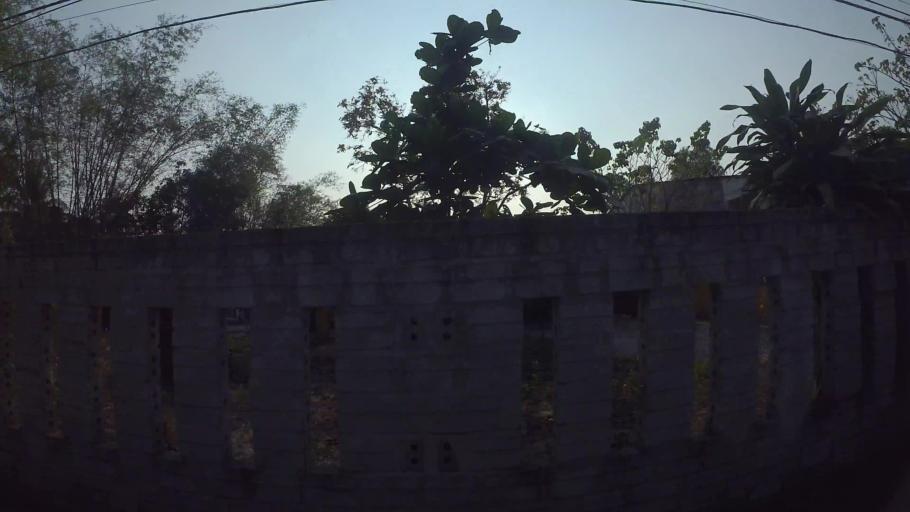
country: VN
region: Da Nang
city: Ngu Hanh Son
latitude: 15.9715
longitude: 108.2438
